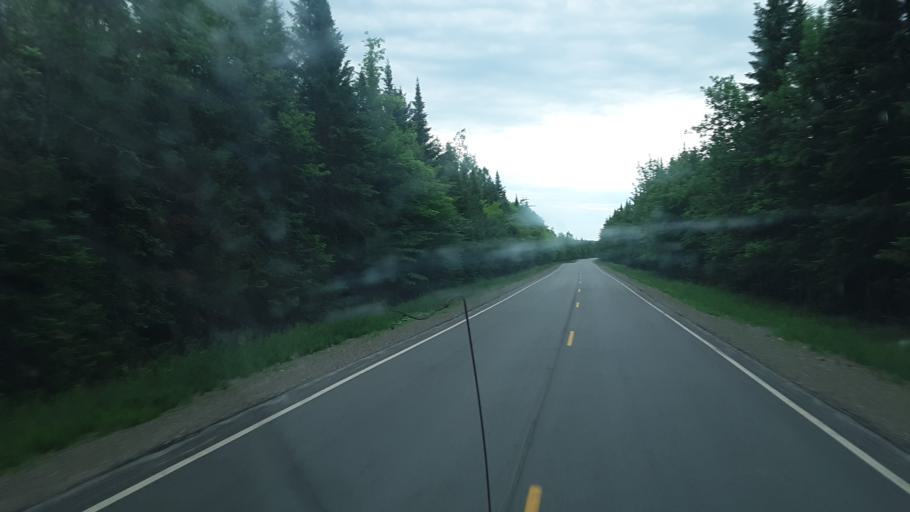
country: US
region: Maine
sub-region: Penobscot County
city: Medway
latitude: 45.7500
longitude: -68.3106
